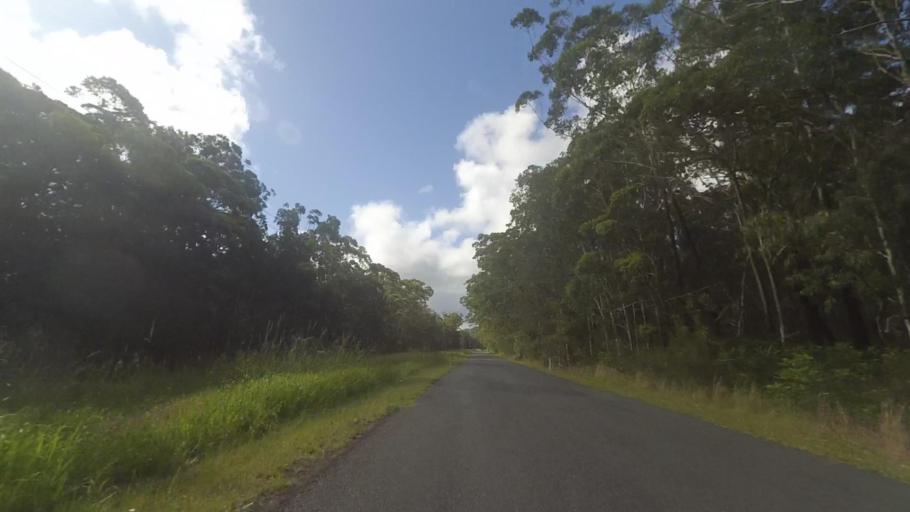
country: AU
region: New South Wales
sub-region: Great Lakes
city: Forster
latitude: -32.4064
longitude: 152.4631
